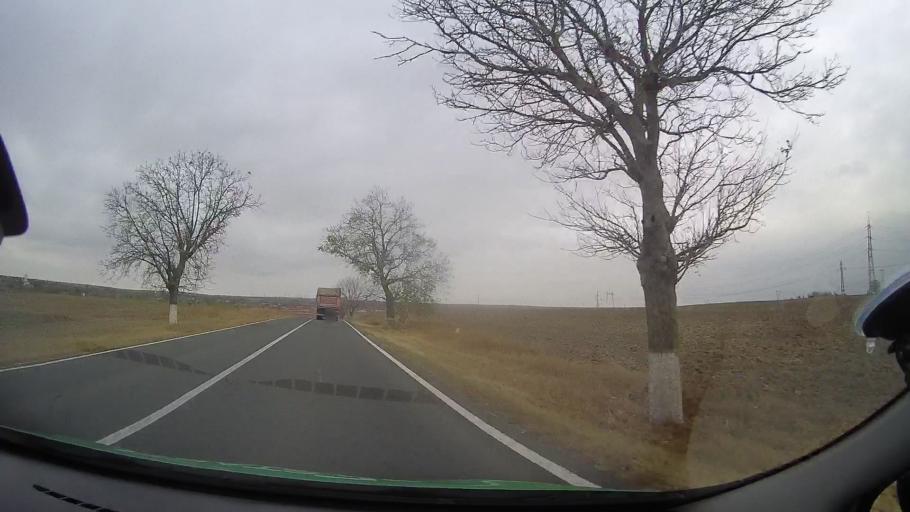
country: RO
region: Constanta
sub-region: Comuna Castelu
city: Castelu
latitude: 44.2566
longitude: 28.3501
